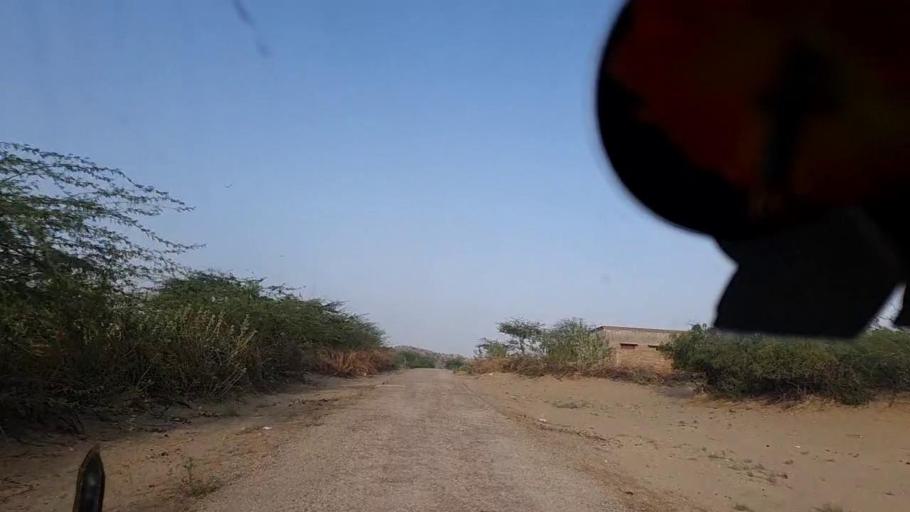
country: PK
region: Sindh
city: Diplo
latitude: 24.5657
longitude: 69.4879
